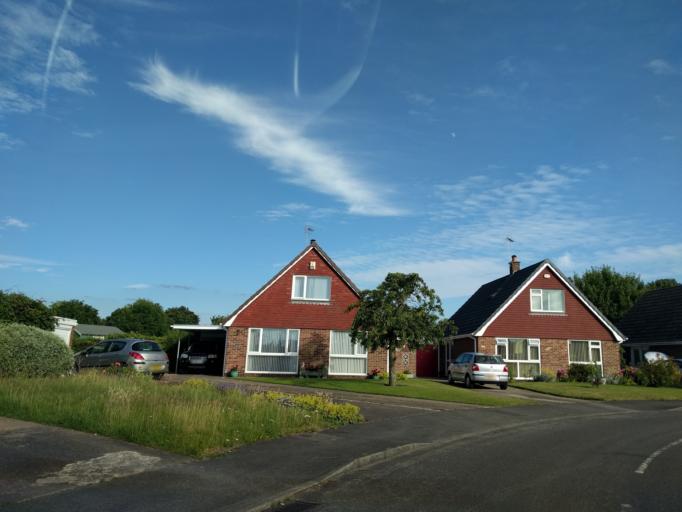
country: GB
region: England
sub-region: Nottinghamshire
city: Newark on Trent
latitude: 53.0687
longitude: -0.7947
